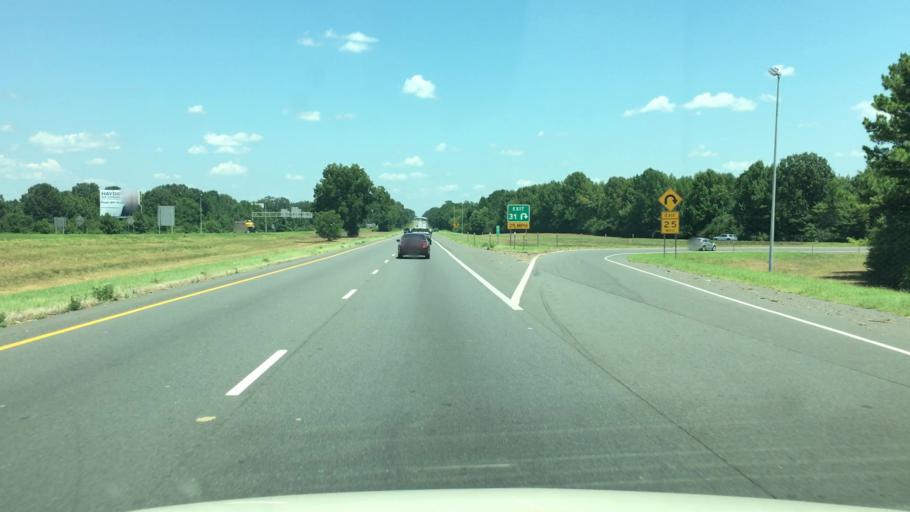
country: US
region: Arkansas
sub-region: Hempstead County
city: Hope
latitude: 33.6913
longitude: -93.5974
